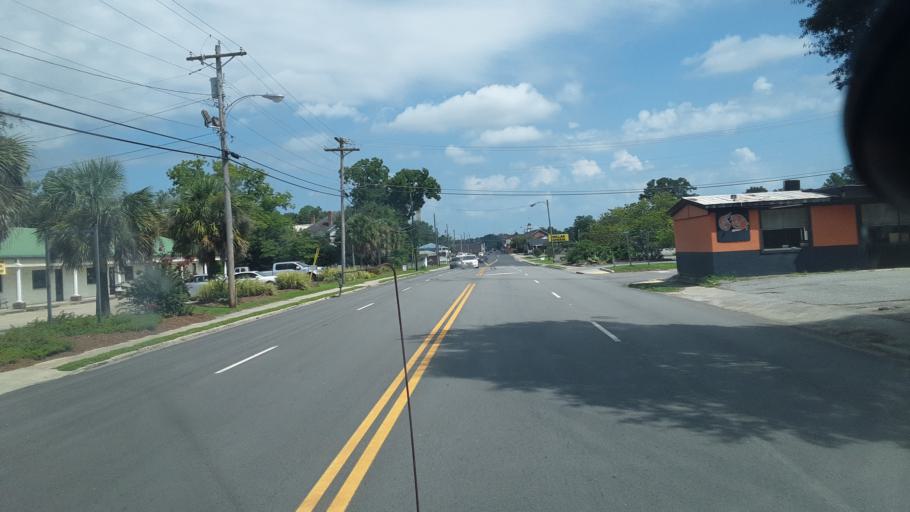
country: US
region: South Carolina
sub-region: Bamberg County
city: Bamberg
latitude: 33.2904
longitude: -81.0375
